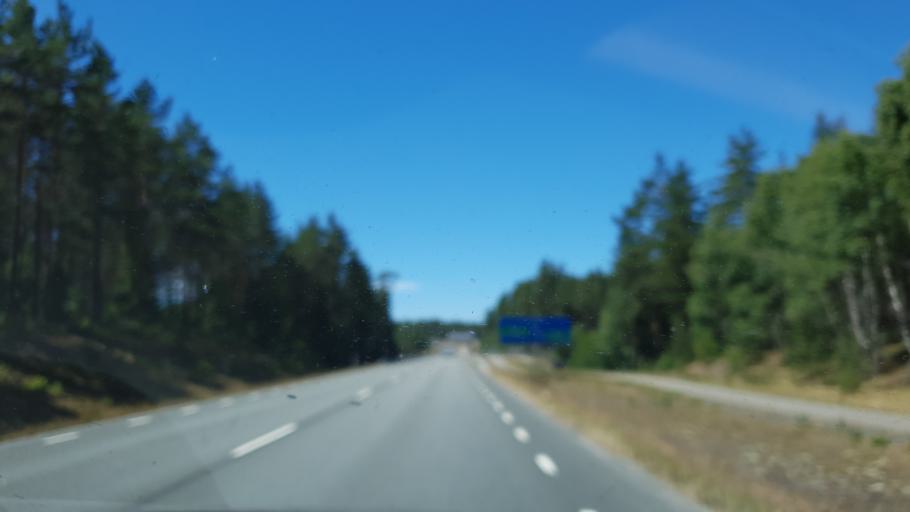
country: SE
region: Joenkoeping
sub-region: Vaggeryds Kommun
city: Vaggeryd
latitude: 57.5265
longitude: 14.1259
